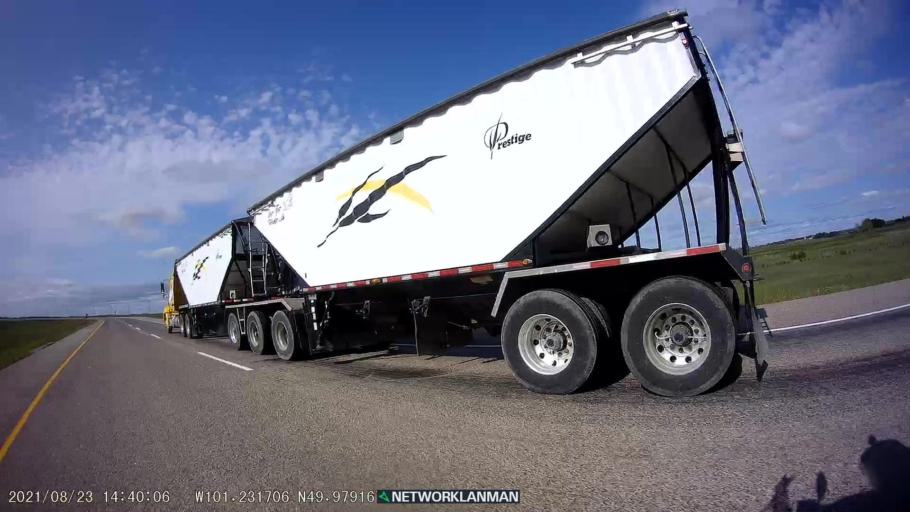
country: CA
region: Manitoba
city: Virden
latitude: 49.9797
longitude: -101.2328
